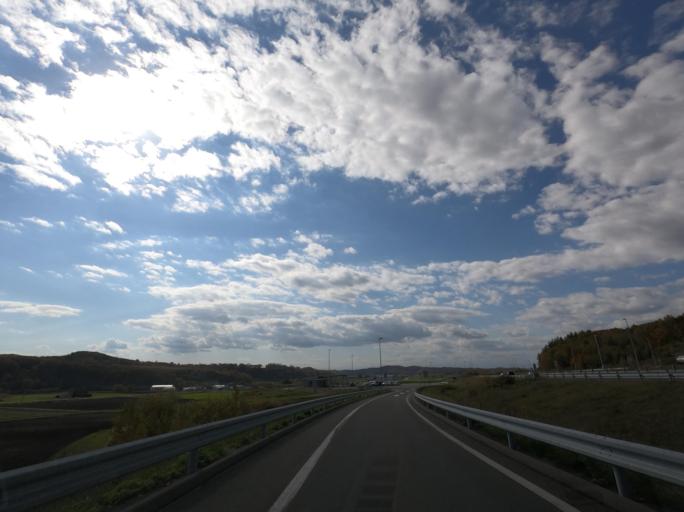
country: JP
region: Hokkaido
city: Otofuke
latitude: 43.1161
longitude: 143.6396
